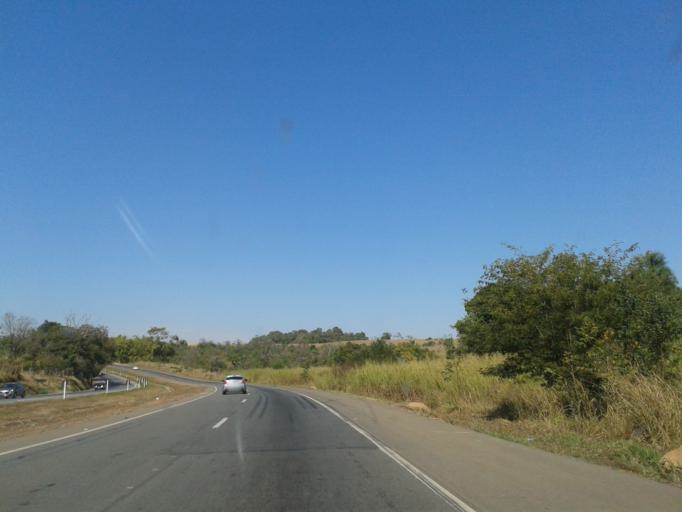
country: BR
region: Goias
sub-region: Piracanjuba
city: Piracanjuba
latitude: -17.2177
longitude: -49.2290
